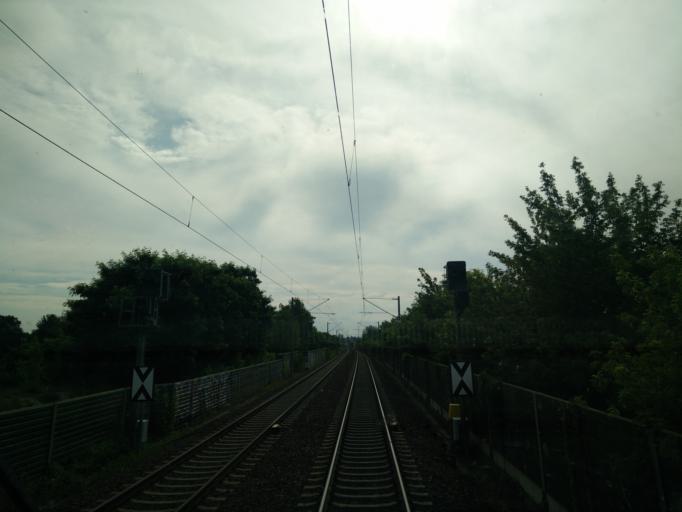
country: DE
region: Berlin
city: Staaken
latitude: 52.5419
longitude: 13.1578
